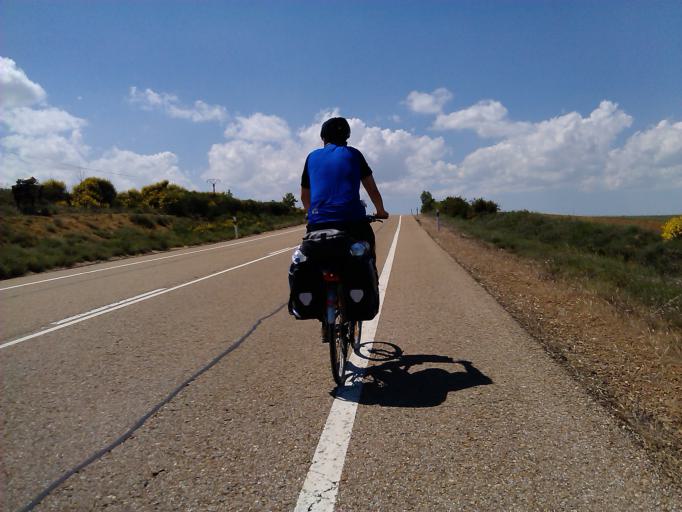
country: ES
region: Castille and Leon
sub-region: Provincia de Palencia
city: Ledigos
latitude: 42.3438
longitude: -4.8446
